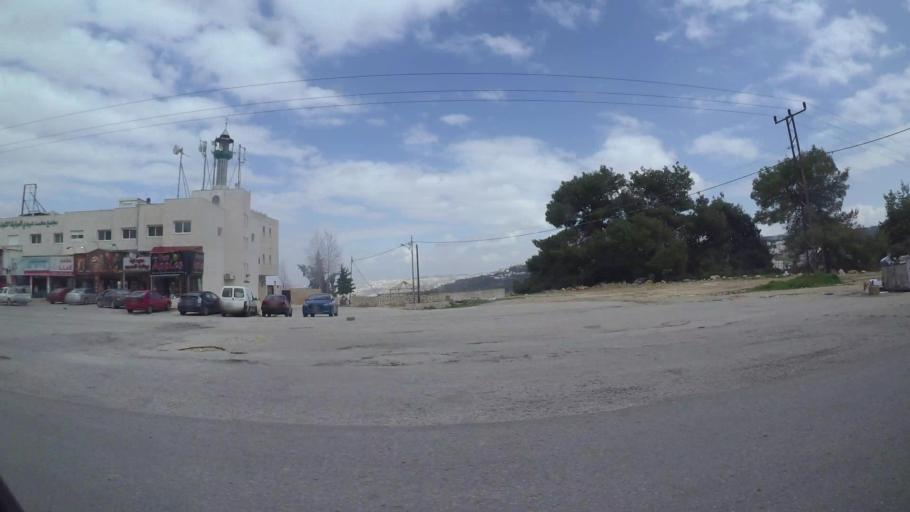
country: JO
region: Balqa
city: As Salt
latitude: 32.0331
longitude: 35.7936
